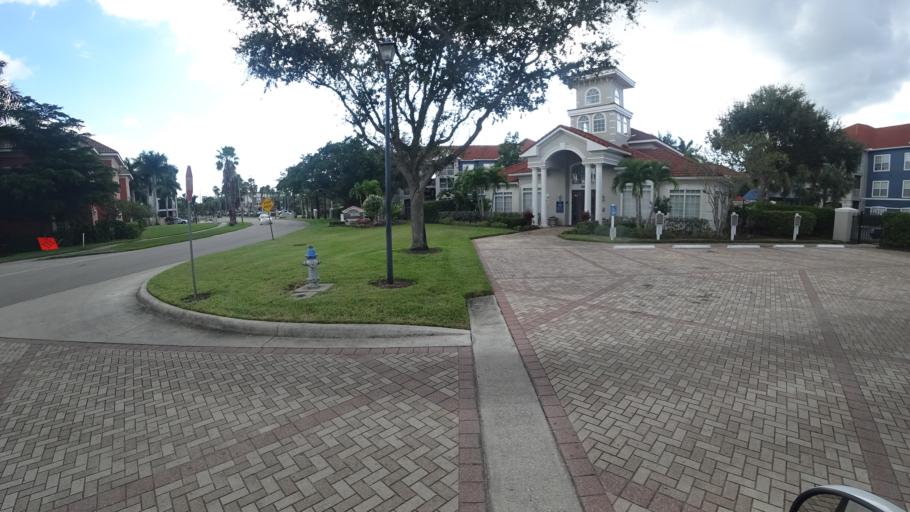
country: US
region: Florida
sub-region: Manatee County
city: Bradenton
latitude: 27.4980
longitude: -82.5652
